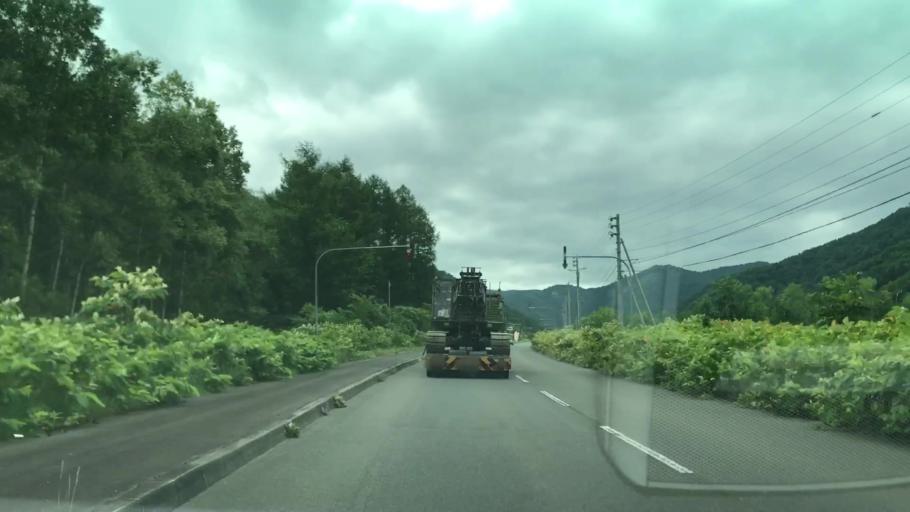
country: JP
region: Hokkaido
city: Yoichi
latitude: 43.0308
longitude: 140.8655
